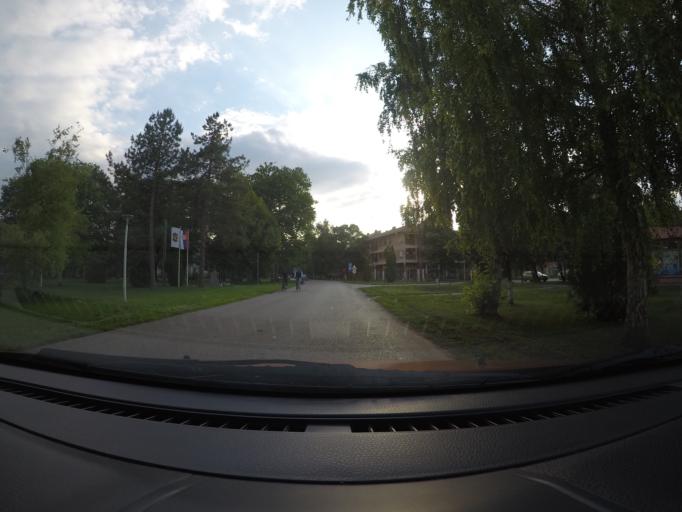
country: RS
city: Debeljaca
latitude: 45.0695
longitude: 20.6019
